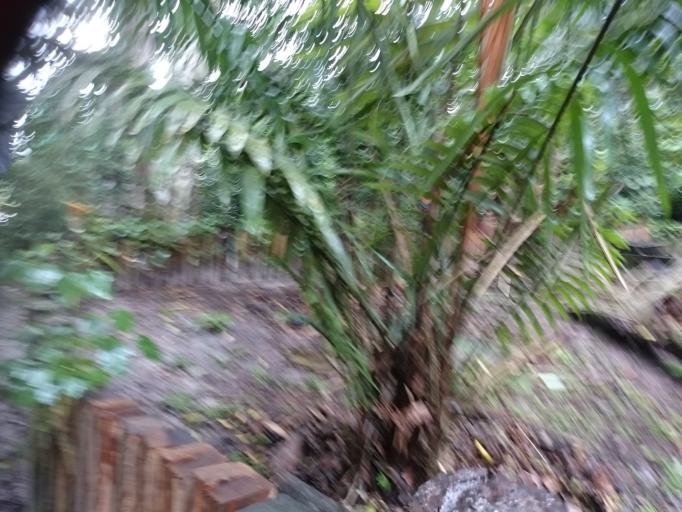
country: PE
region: Loreto
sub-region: Provincia de Maynas
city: Iquitos
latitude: -3.8178
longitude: -73.3223
